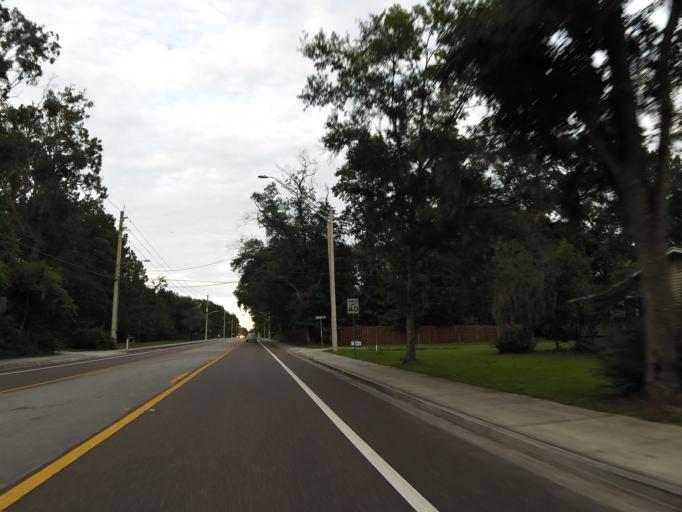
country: US
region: Florida
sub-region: Duval County
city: Baldwin
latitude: 30.3019
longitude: -81.8281
